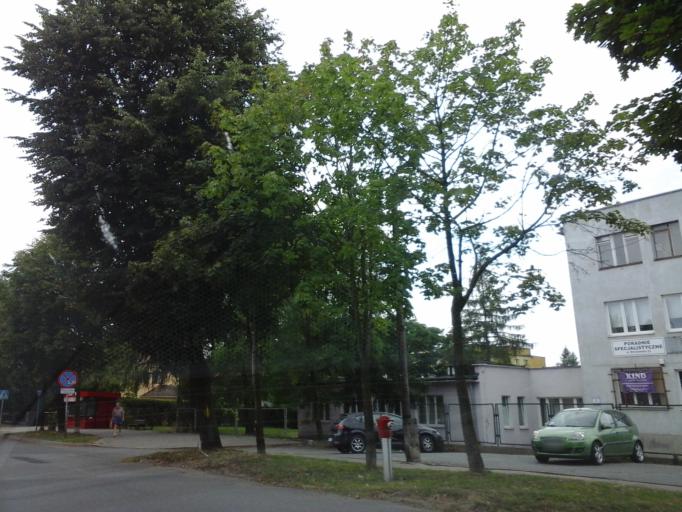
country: PL
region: Lower Silesian Voivodeship
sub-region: Powiat zabkowicki
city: Zabkowice Slaskie
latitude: 50.5993
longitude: 16.8189
